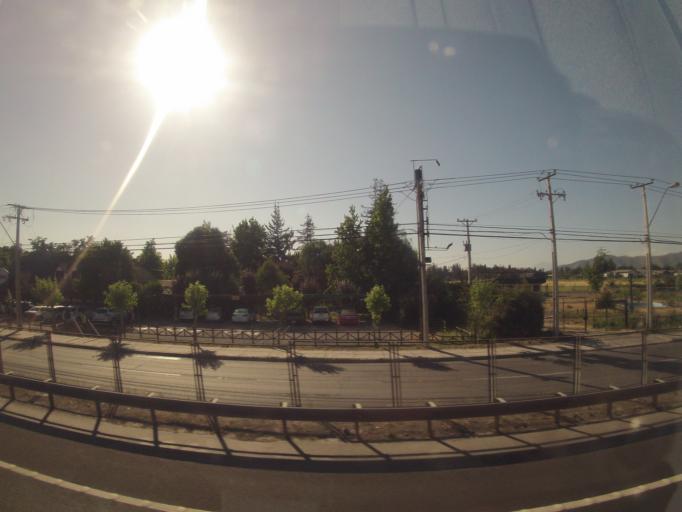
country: CL
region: Santiago Metropolitan
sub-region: Provincia de Maipo
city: San Bernardo
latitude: -33.6581
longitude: -70.7164
